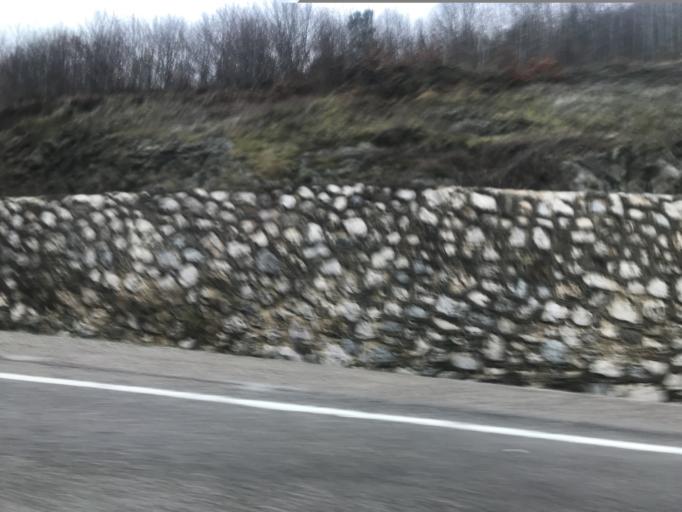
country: TR
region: Bartin
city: Amasra
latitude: 41.6999
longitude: 32.3840
